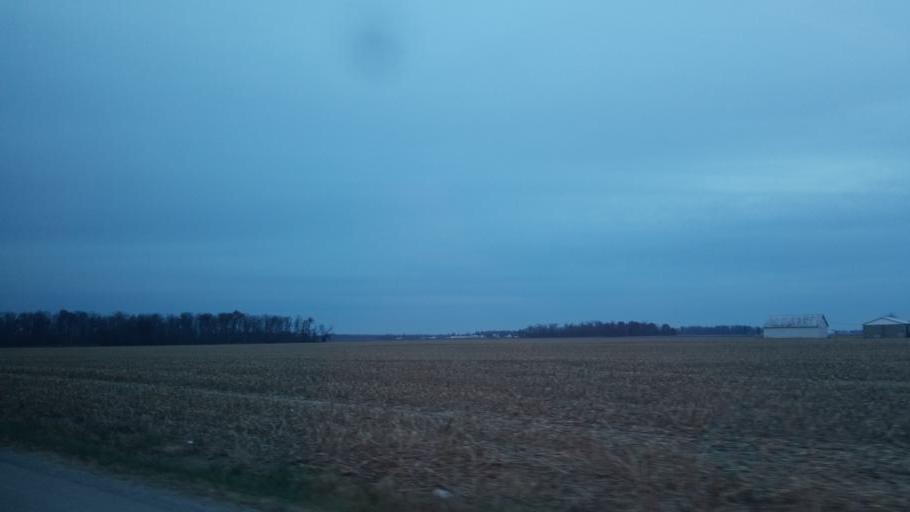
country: US
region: Indiana
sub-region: Adams County
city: Berne
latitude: 40.7446
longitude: -84.9949
